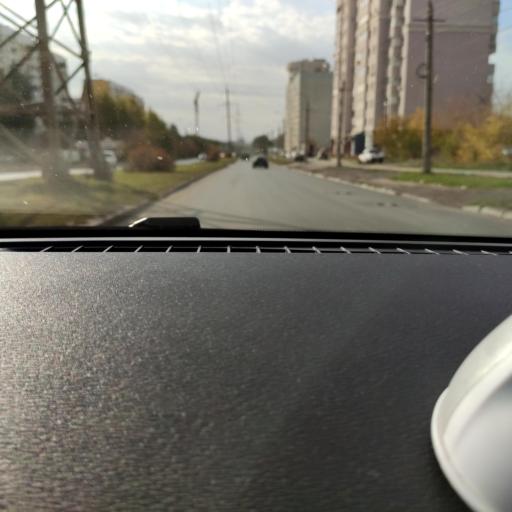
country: RU
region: Samara
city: Samara
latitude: 53.2108
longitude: 50.2131
